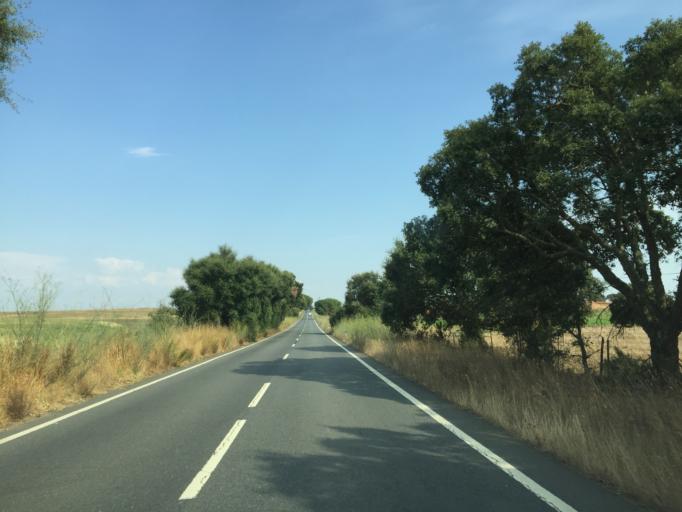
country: PT
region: Beja
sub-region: Aljustrel
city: Aljustrel
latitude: 37.9327
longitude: -8.3504
